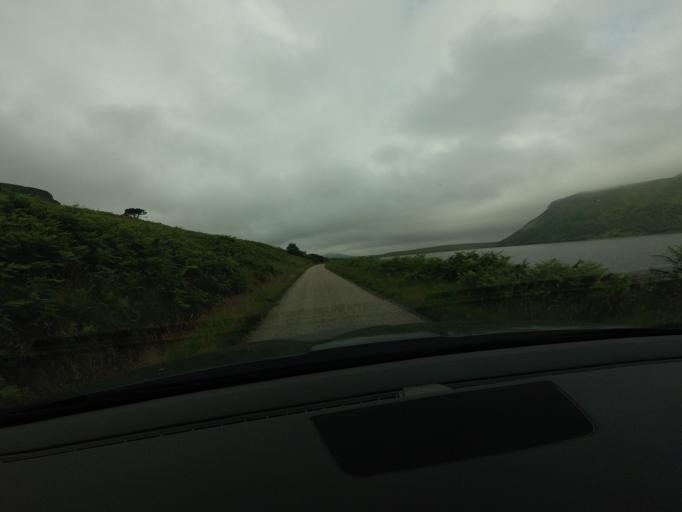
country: GB
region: Scotland
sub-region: Highland
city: Golspie
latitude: 58.4105
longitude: -4.3736
